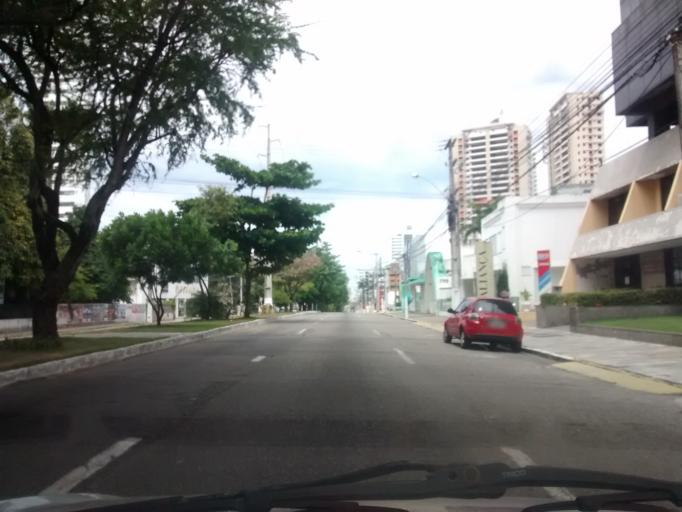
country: BR
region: Rio Grande do Norte
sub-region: Natal
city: Natal
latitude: -5.7897
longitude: -35.2021
